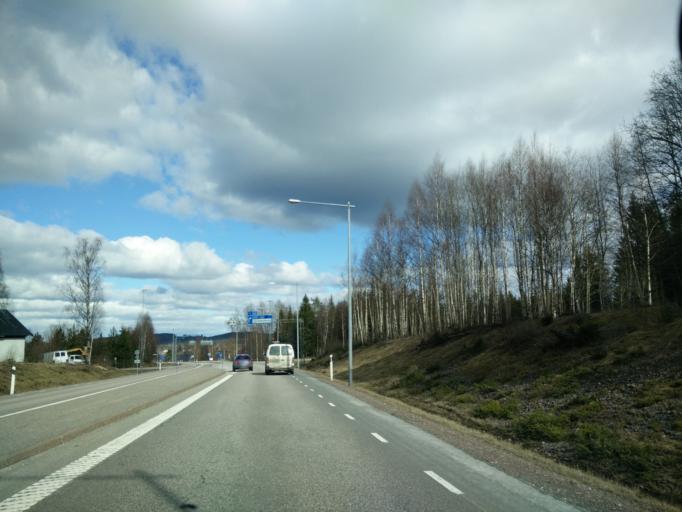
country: SE
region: Vaermland
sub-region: Hagfors Kommun
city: Hagfors
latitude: 59.9938
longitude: 13.5959
